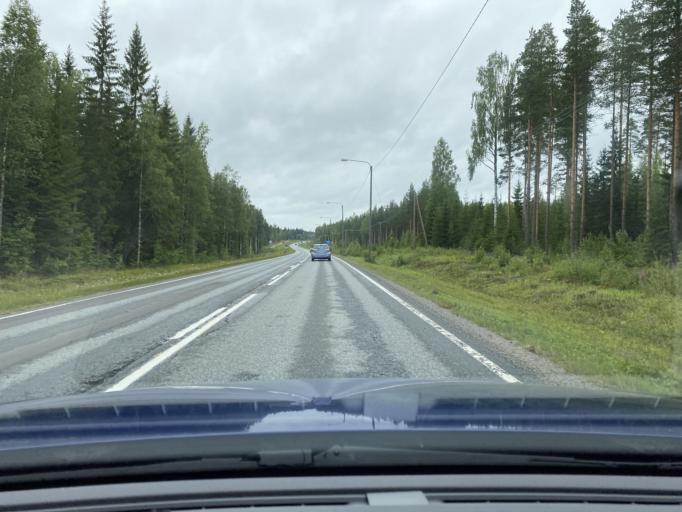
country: FI
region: Central Finland
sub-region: Keuruu
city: Keuruu
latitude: 62.2400
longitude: 24.4886
